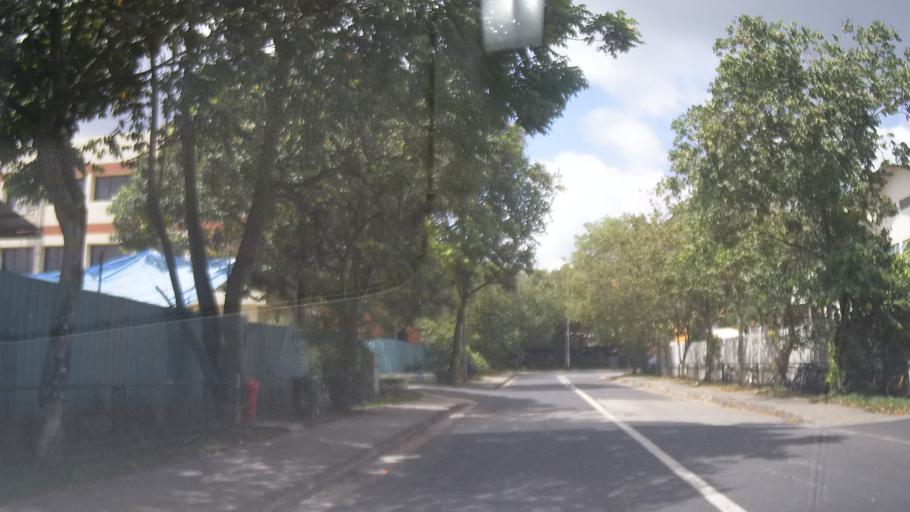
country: MY
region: Johor
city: Johor Bahru
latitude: 1.4279
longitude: 103.7491
